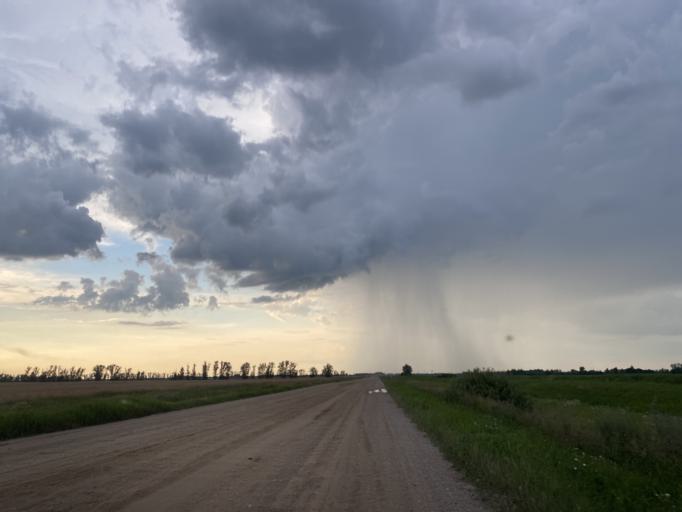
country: BY
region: Brest
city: Tsyelyakhany
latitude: 52.4644
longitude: 25.5714
